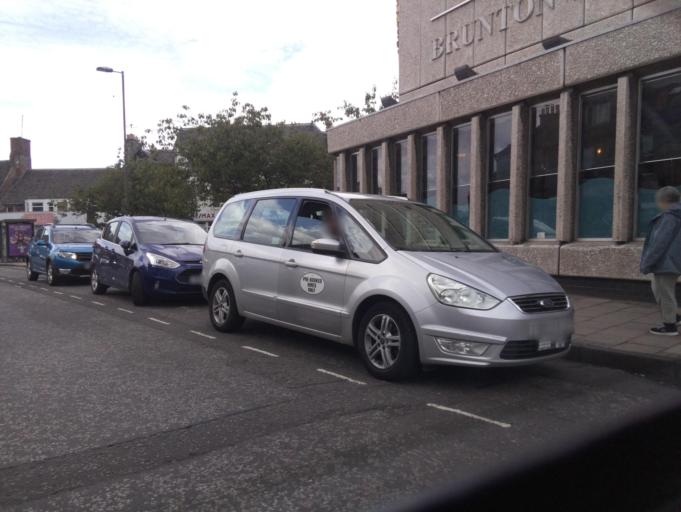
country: GB
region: Scotland
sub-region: East Lothian
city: Musselburgh
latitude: 55.9441
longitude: -3.0580
